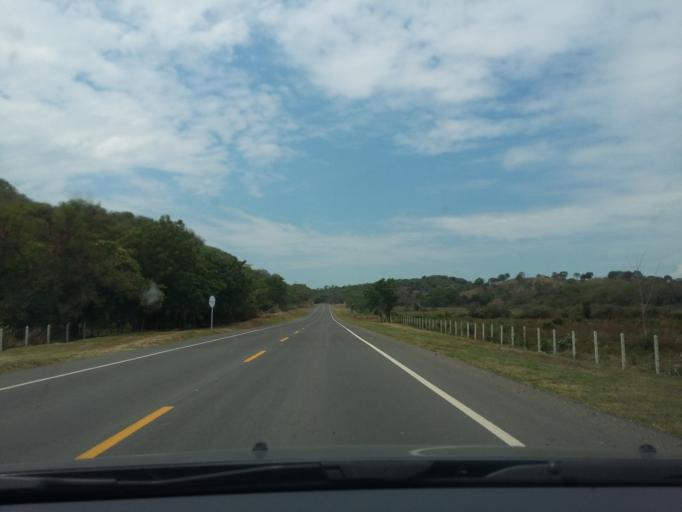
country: CO
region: Tolima
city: Ambalema
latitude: 4.8609
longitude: -74.7408
